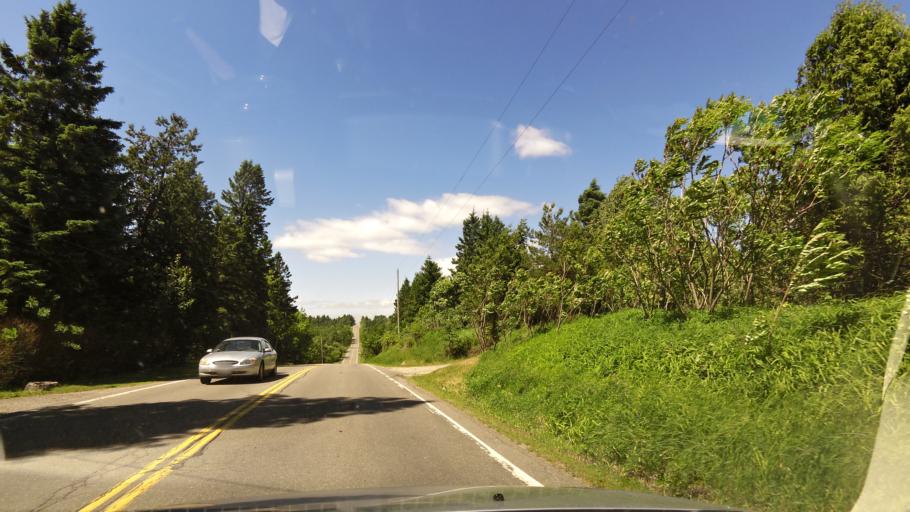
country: CA
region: Ontario
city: Newmarket
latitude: 43.9763
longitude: -79.5413
